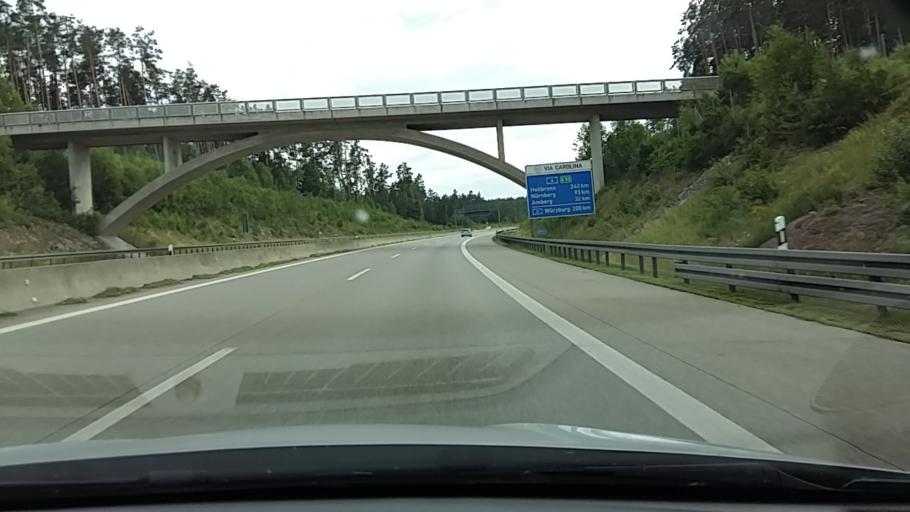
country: DE
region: Bavaria
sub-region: Upper Palatinate
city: Pfreimd
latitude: 49.5080
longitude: 12.1607
